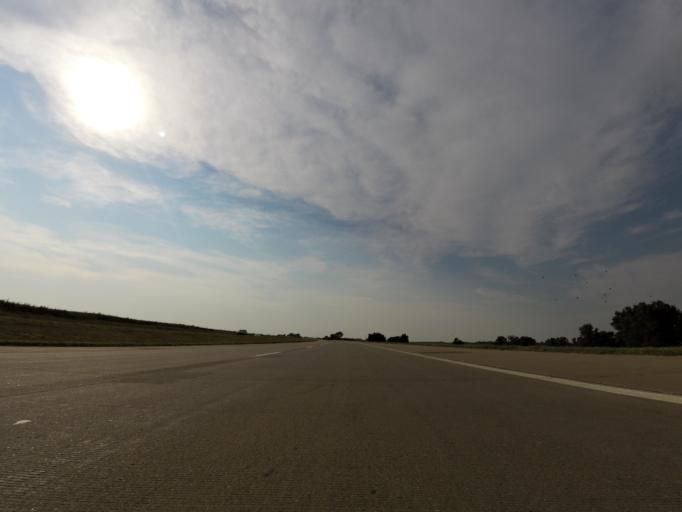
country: US
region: Kansas
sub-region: Sedgwick County
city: Colwich
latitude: 37.8414
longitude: -97.5757
